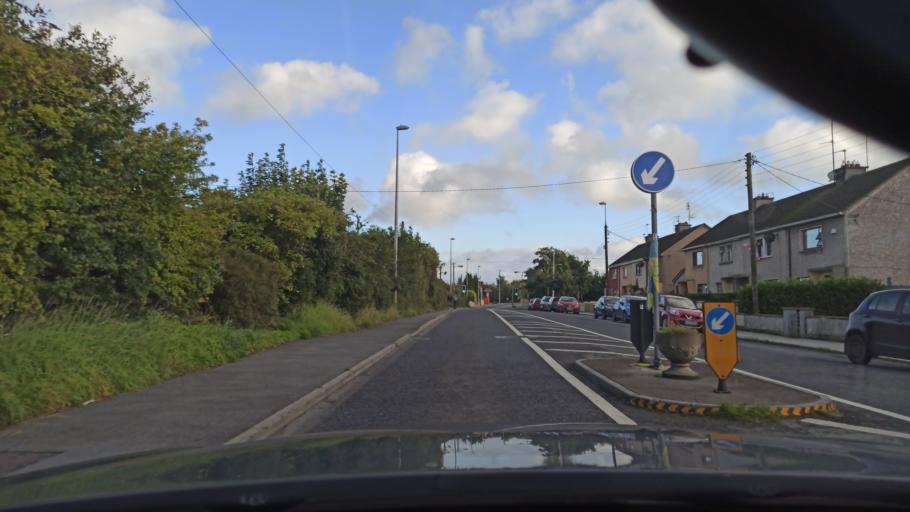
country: IE
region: Munster
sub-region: North Tipperary
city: Roscrea
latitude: 52.9416
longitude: -7.7895
